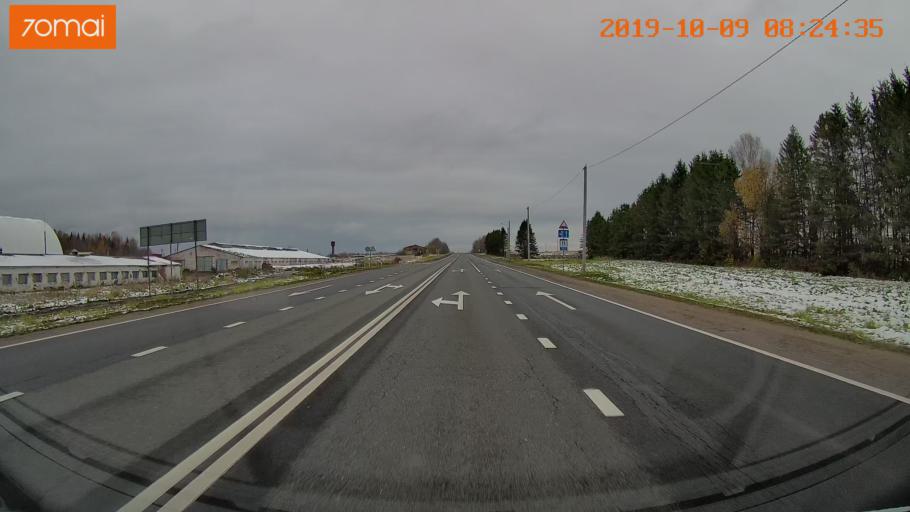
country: RU
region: Vologda
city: Gryazovets
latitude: 58.7683
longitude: 40.2776
